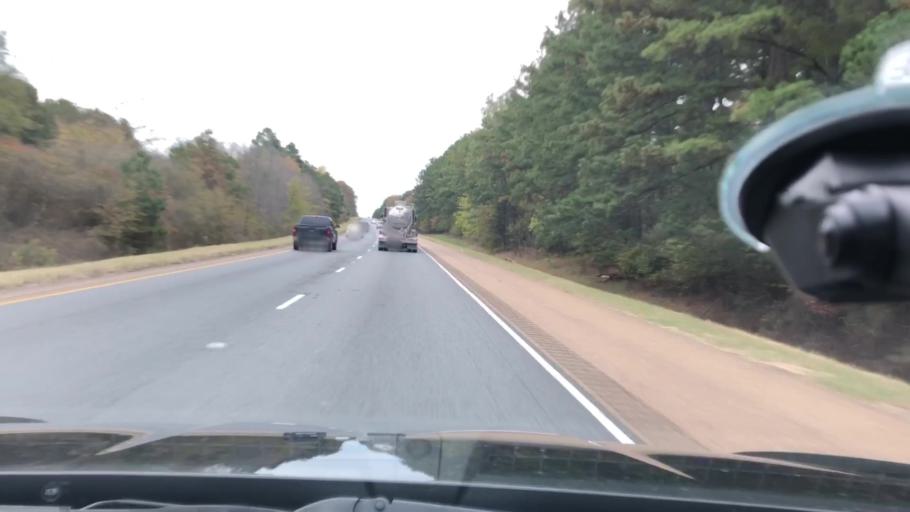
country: US
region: Arkansas
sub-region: Clark County
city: Gurdon
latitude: 33.9329
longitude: -93.2552
